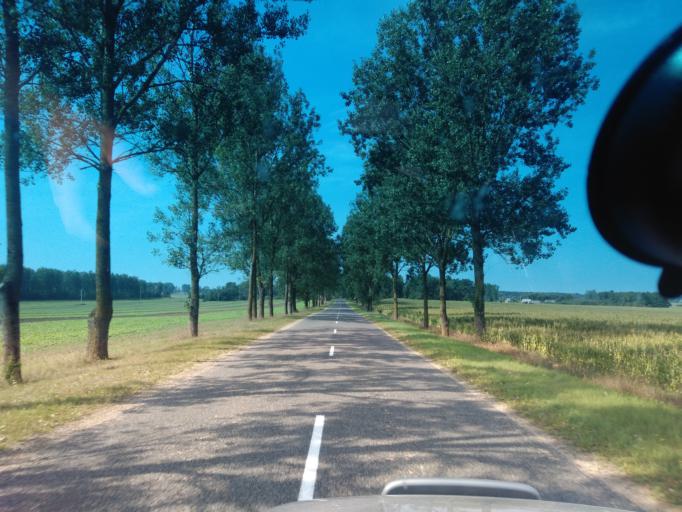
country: BY
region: Minsk
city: Kapyl'
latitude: 53.2715
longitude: 27.2180
